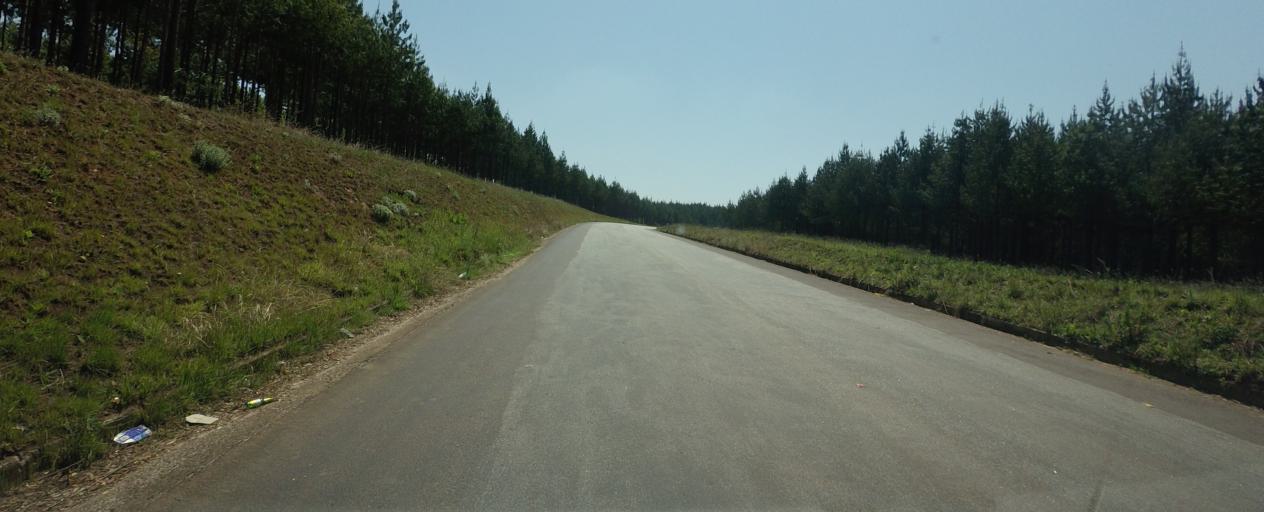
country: ZA
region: Mpumalanga
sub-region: Ehlanzeni District
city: Graksop
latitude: -24.9139
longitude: 30.8433
